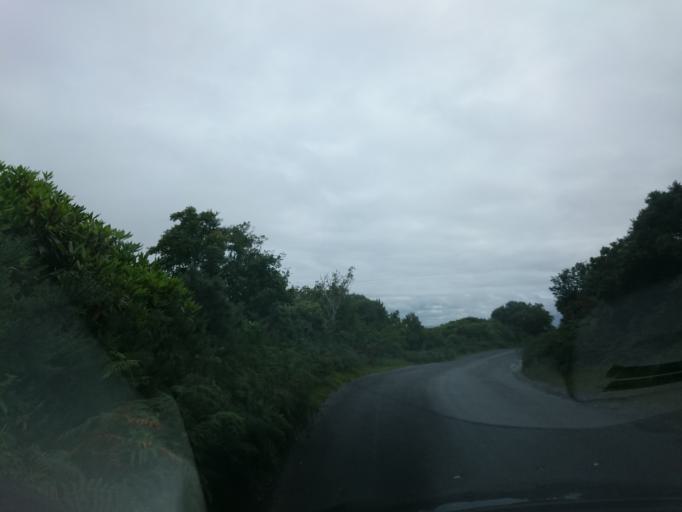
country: IE
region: Connaught
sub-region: Maigh Eo
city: Westport
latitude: 53.9044
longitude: -9.7885
